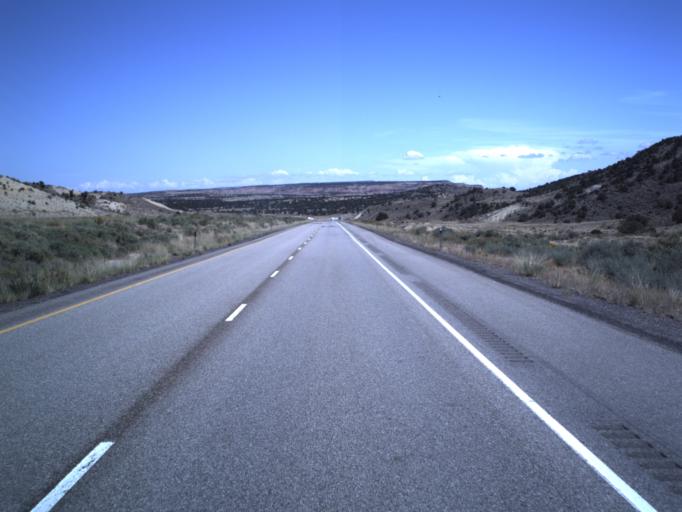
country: US
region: Utah
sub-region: Emery County
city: Ferron
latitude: 38.7917
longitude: -111.2943
